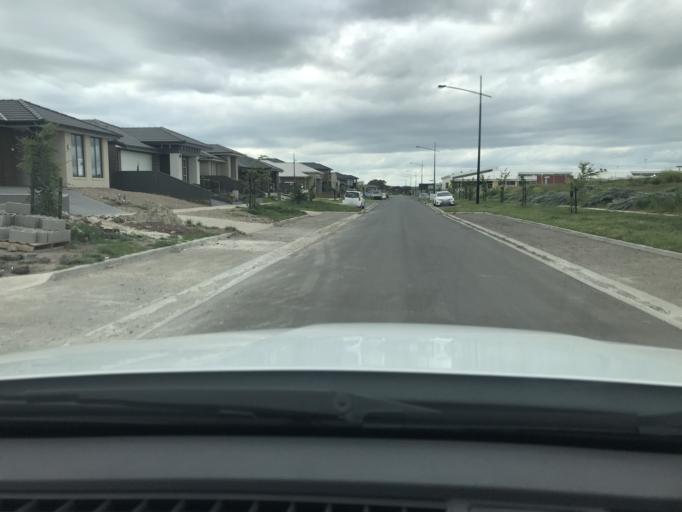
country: AU
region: Victoria
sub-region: Hume
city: Greenvale
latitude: -37.6008
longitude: 144.8880
